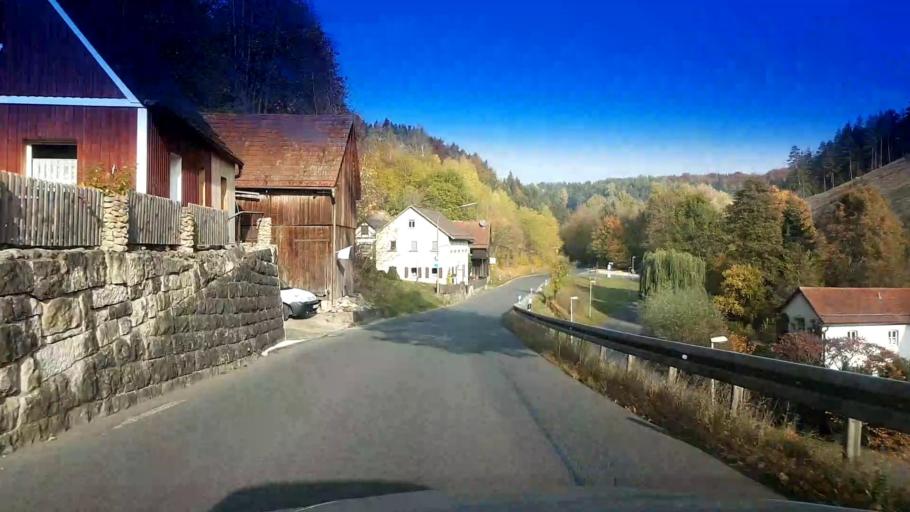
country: DE
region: Bavaria
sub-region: Upper Franconia
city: Stadelhofen
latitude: 50.0216
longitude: 11.1994
